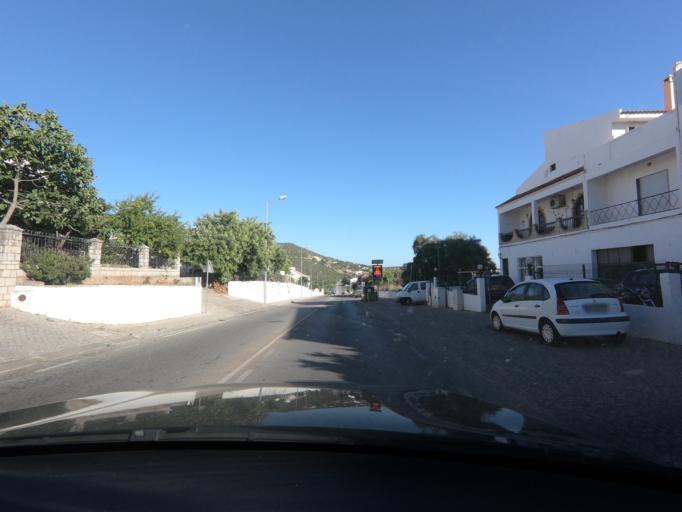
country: PT
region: Faro
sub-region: Loule
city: Loule
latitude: 37.1220
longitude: -8.0143
